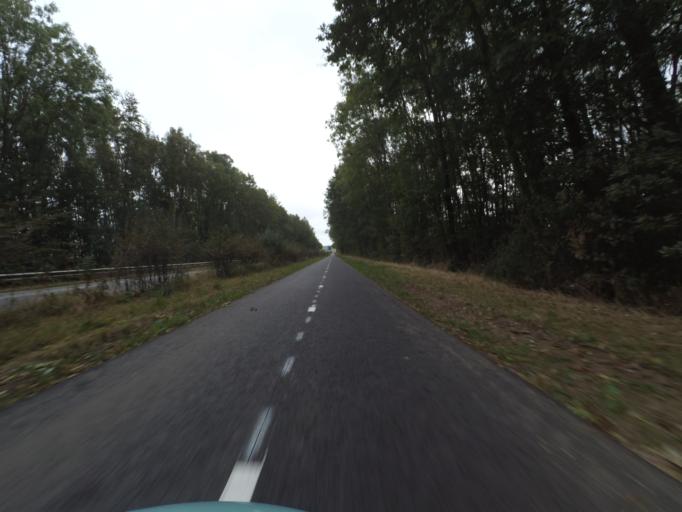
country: NL
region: Gelderland
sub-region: Gemeente Tiel
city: Tiel
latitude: 51.9265
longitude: 5.4302
